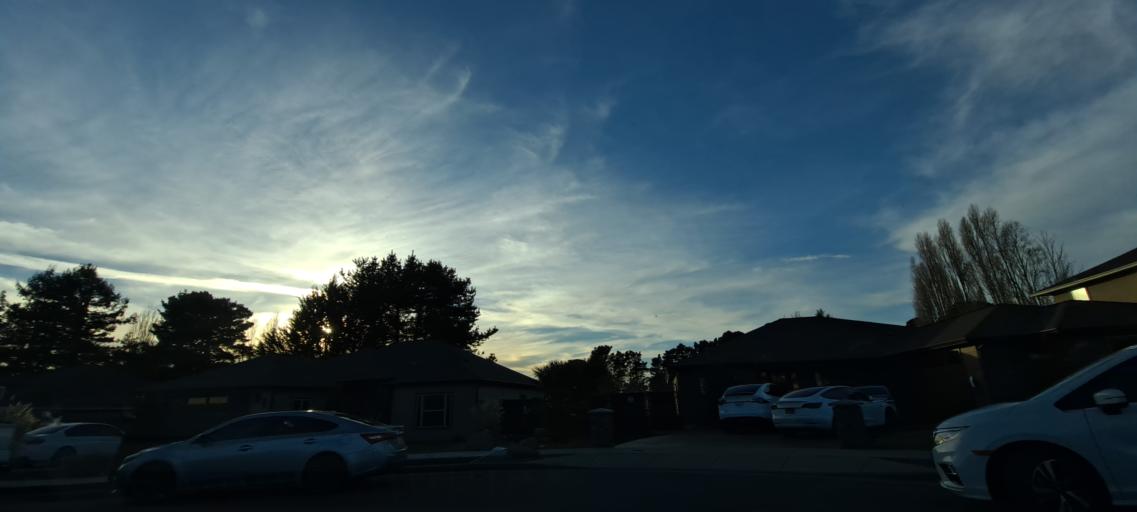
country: US
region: California
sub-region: Humboldt County
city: Fortuna
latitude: 40.5793
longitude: -124.1368
